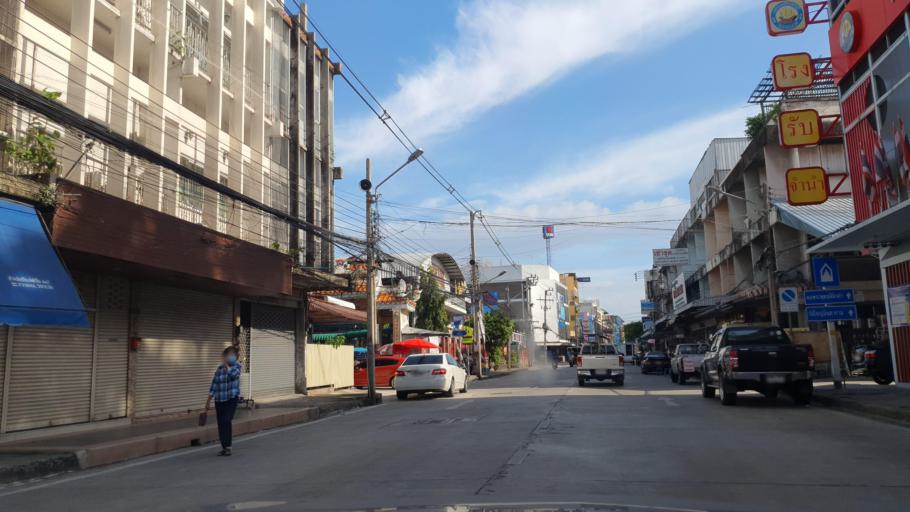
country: TH
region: Chon Buri
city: Chon Buri
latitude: 13.3688
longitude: 100.9888
